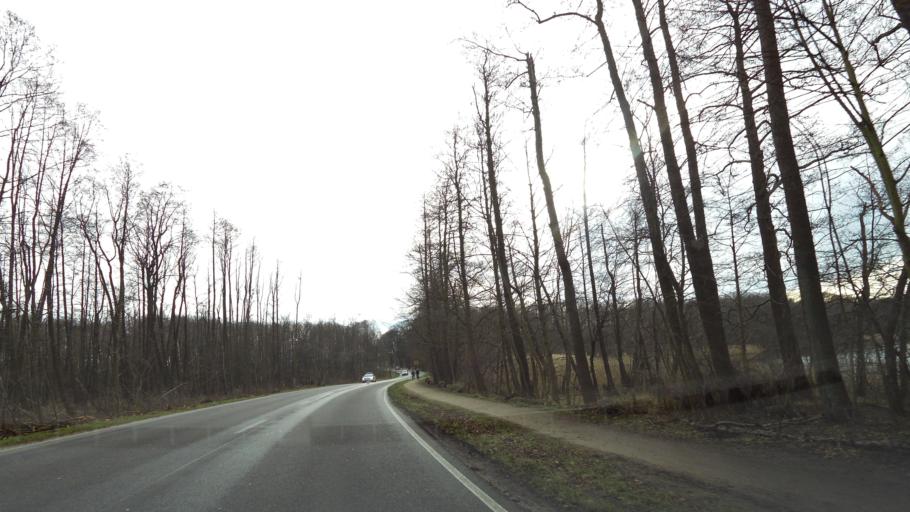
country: DE
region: Brandenburg
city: Strausberg
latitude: 52.5915
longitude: 13.8929
